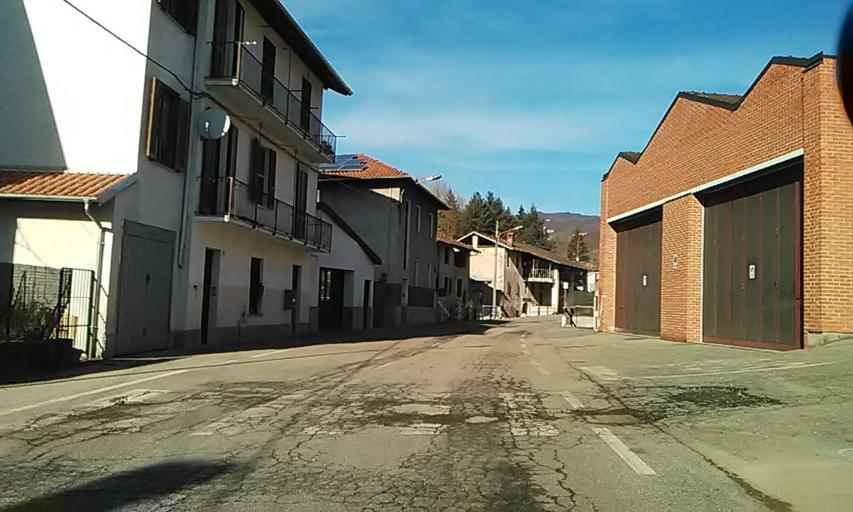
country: IT
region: Piedmont
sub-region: Provincia di Vercelli
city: Borgosesia
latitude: 45.7309
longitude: 8.2990
